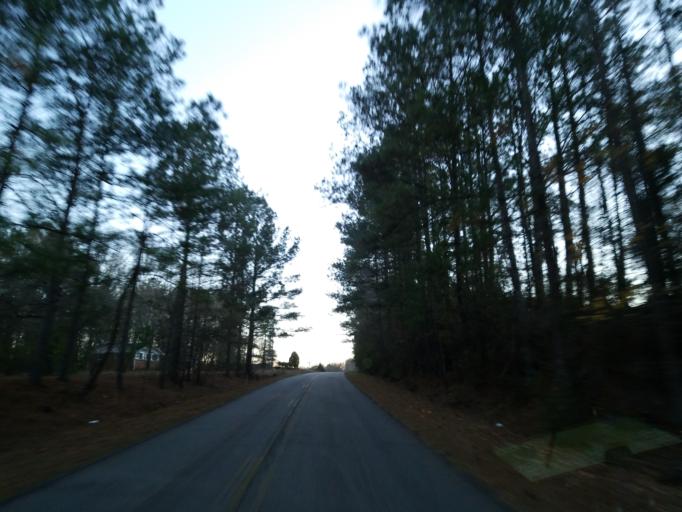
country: US
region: Georgia
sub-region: Monroe County
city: Forsyth
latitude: 32.9906
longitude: -83.8792
